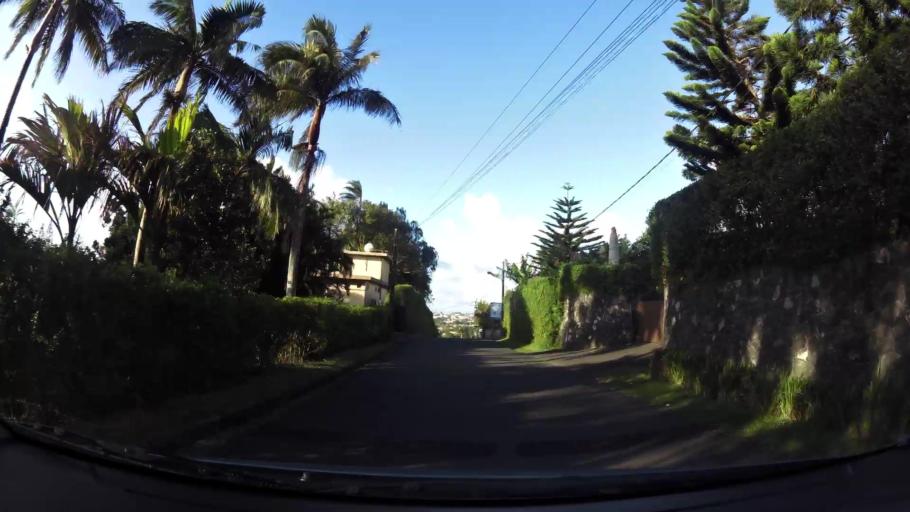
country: MU
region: Plaines Wilhems
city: Curepipe
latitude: -20.3159
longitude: 57.5107
